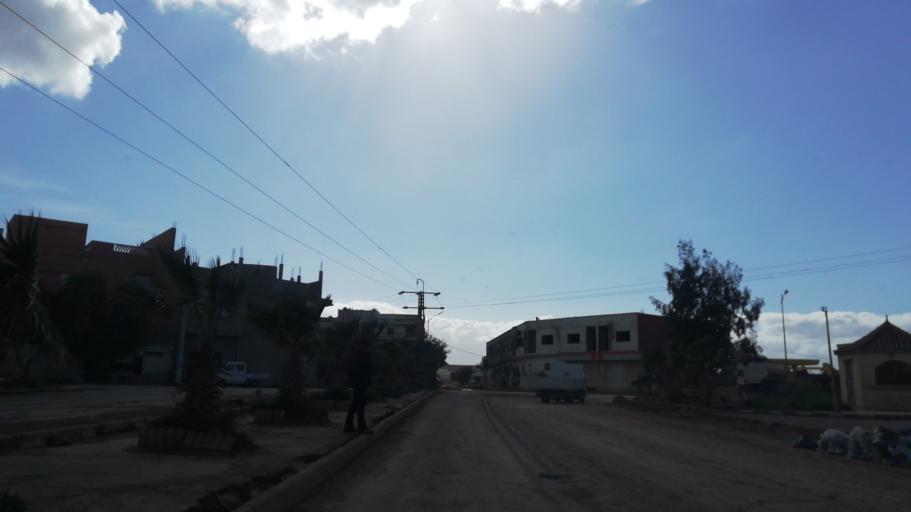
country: DZ
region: Oran
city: Es Senia
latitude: 35.6231
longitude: -0.5841
